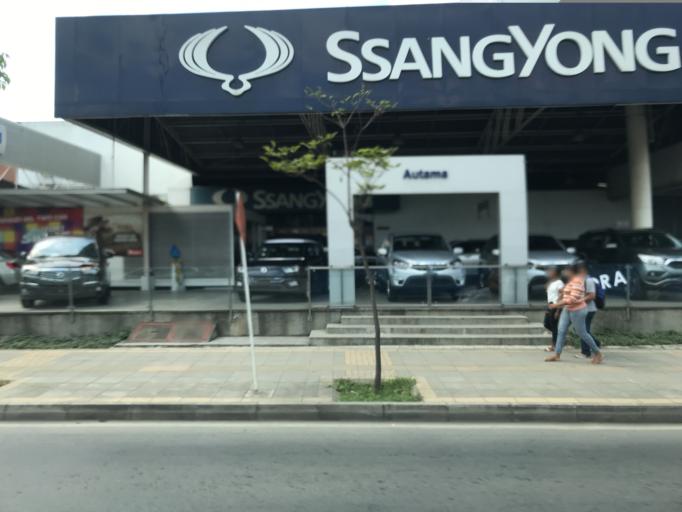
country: CO
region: Valle del Cauca
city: Cali
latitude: 3.4893
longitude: -76.5107
